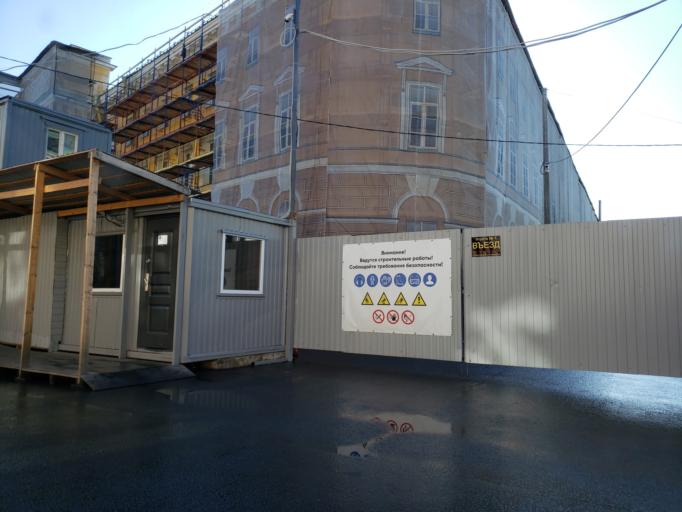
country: RU
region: St.-Petersburg
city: Saint Petersburg
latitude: 59.9443
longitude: 30.3258
